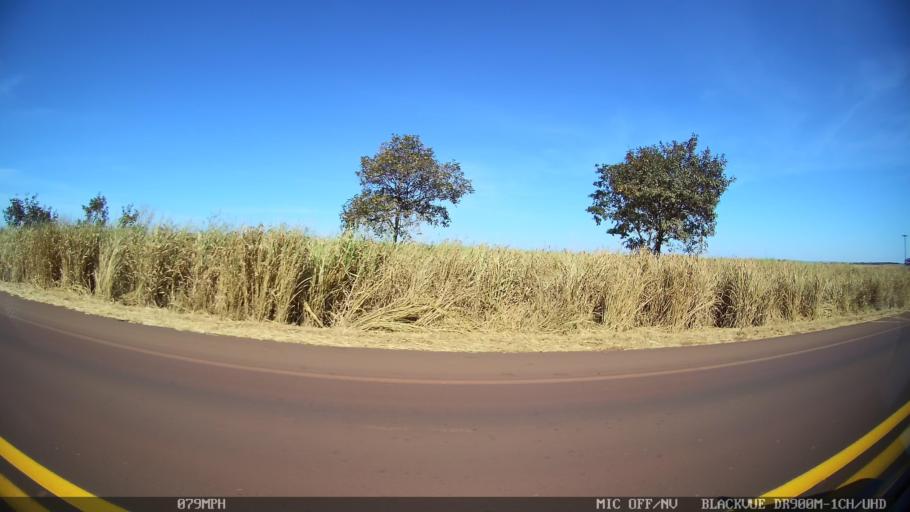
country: BR
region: Sao Paulo
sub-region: Barretos
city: Barretos
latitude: -20.4653
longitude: -48.4751
